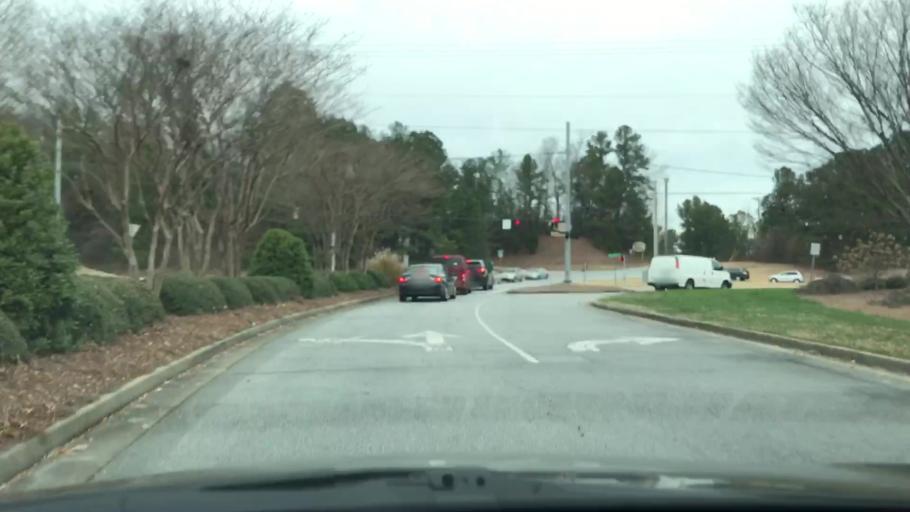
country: US
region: Georgia
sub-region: Gwinnett County
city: Norcross
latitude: 33.9327
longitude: -84.1742
